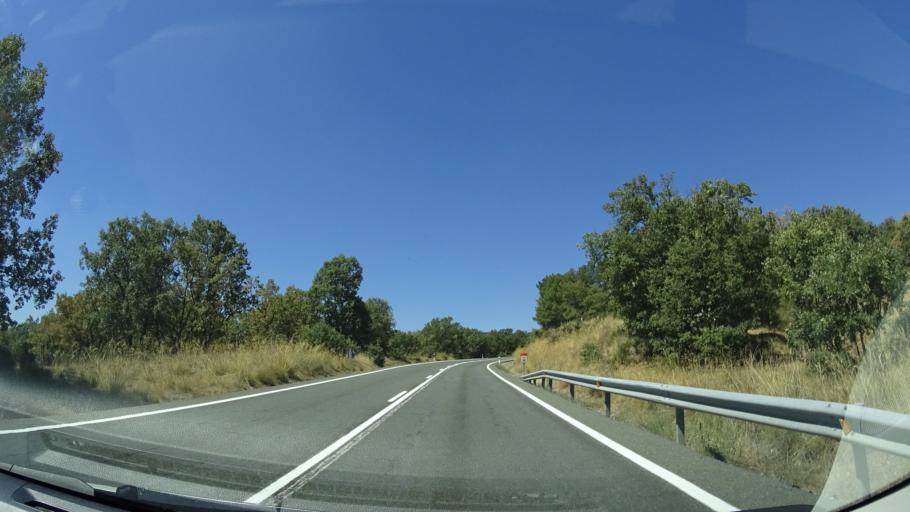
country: ES
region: Castille and Leon
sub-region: Provincia de Avila
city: Navalperal de Pinares
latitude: 40.5949
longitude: -4.4526
